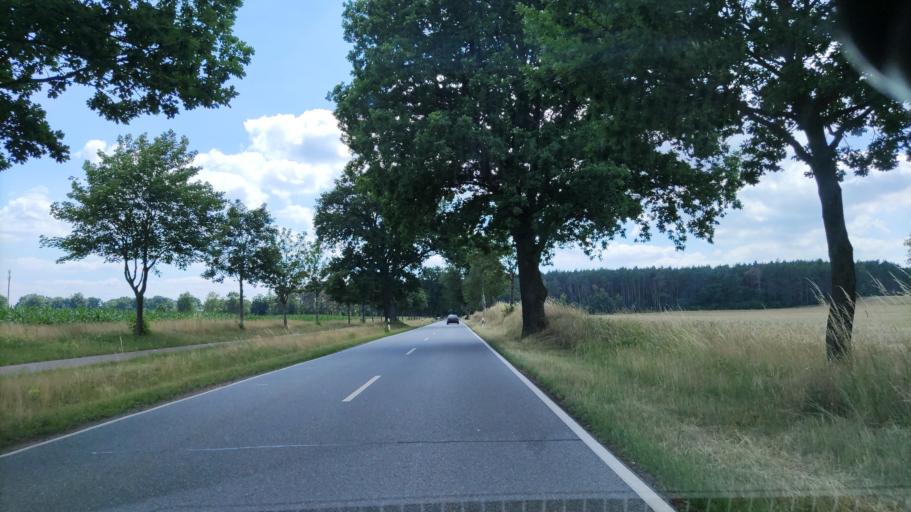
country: DE
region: Mecklenburg-Vorpommern
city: Hagenow
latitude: 53.3892
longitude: 11.1620
